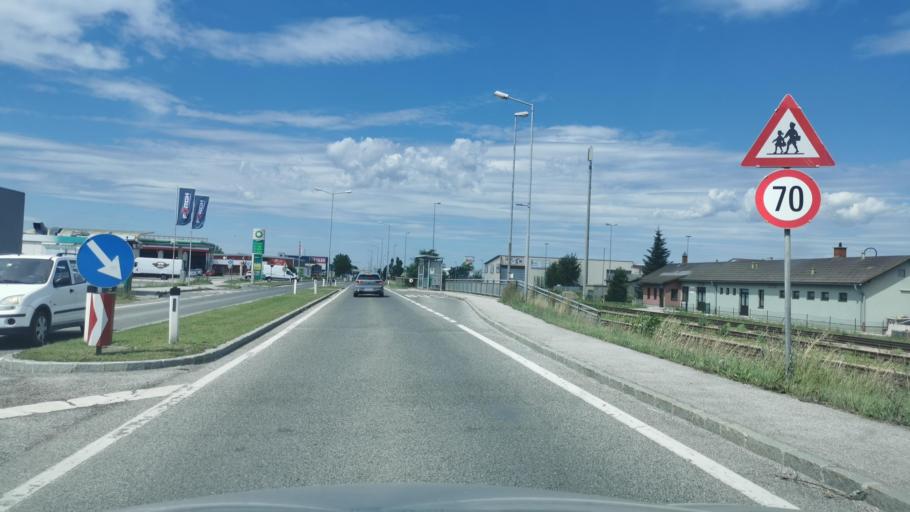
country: AT
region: Lower Austria
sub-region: Sankt Polten Stadt
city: Sankt Poelten
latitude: 48.1564
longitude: 15.6147
